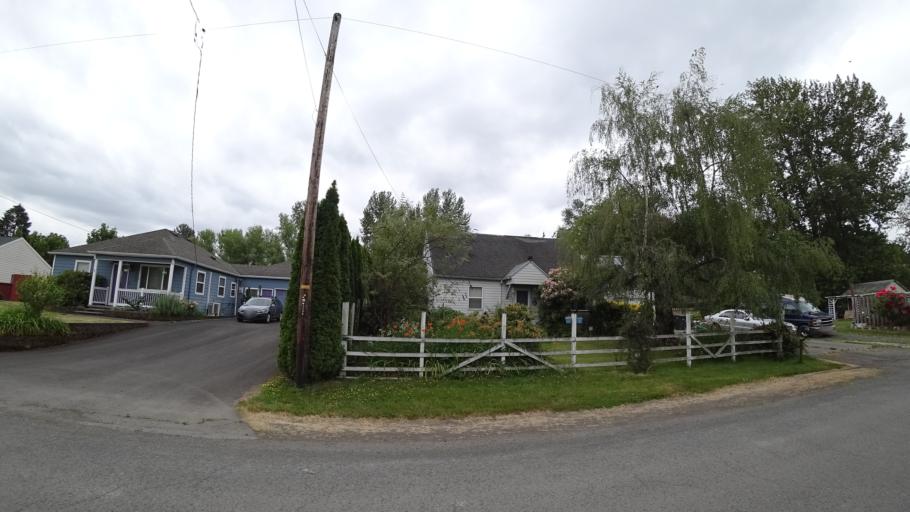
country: US
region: Washington
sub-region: Clark County
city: Vancouver
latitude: 45.5931
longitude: -122.6534
